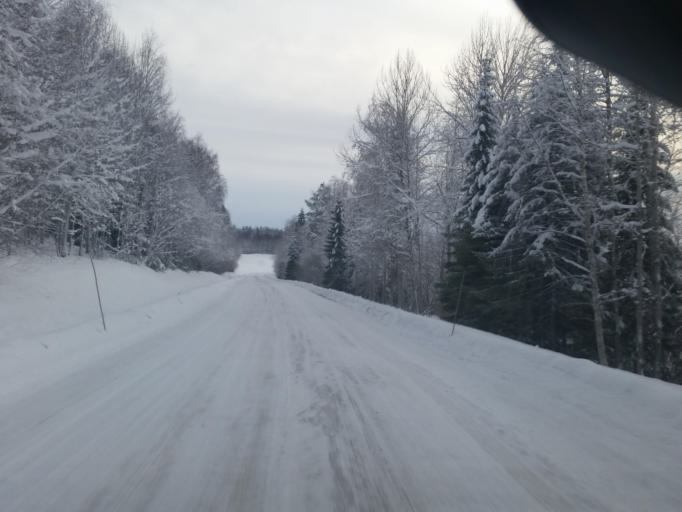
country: SE
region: Norrbotten
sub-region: Pitea Kommun
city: Norrfjarden
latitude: 65.6079
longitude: 21.4146
